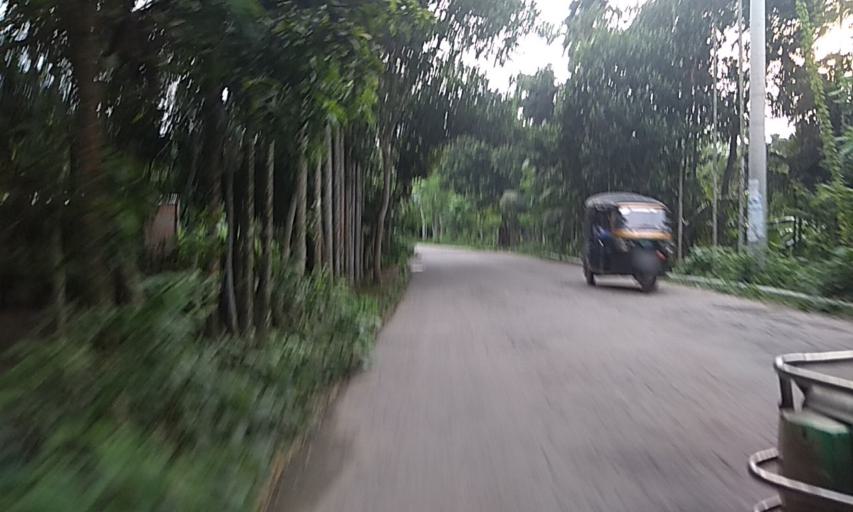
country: BD
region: Dhaka
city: Dohar
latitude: 23.4599
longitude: 89.9868
